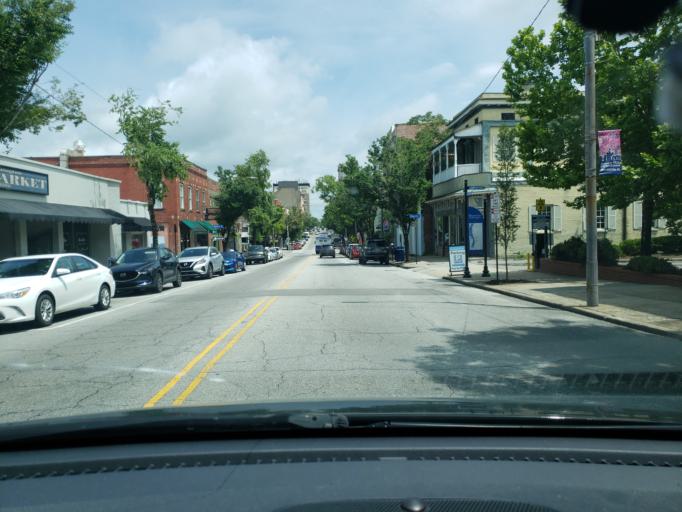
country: US
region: North Carolina
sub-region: New Hanover County
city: Wilmington
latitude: 34.2332
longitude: -77.9485
